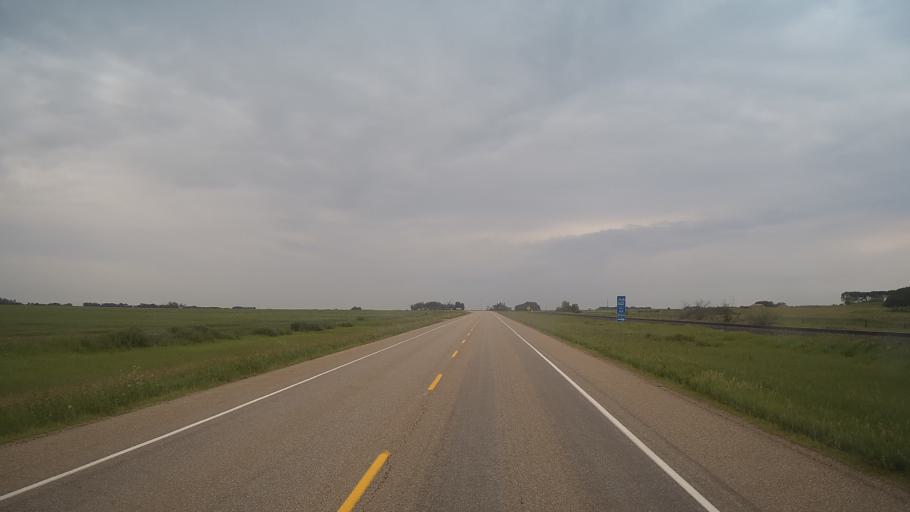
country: CA
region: Saskatchewan
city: Langham
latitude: 52.1265
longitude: -107.2802
